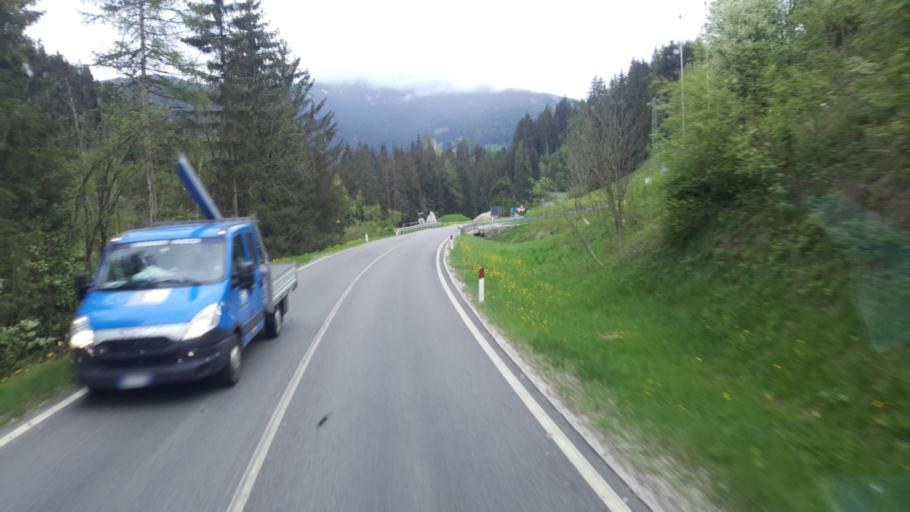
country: IT
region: Trentino-Alto Adige
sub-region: Bolzano
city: Monguelfo
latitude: 46.7660
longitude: 12.1193
